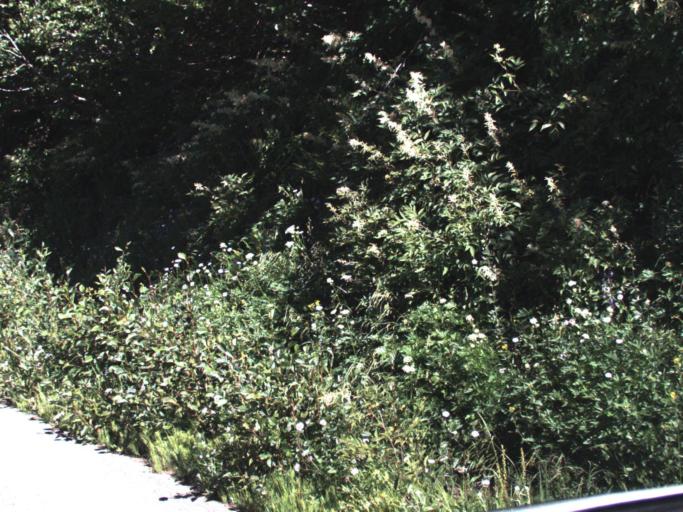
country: US
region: Washington
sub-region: King County
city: Enumclaw
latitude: 46.8684
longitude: -121.5283
